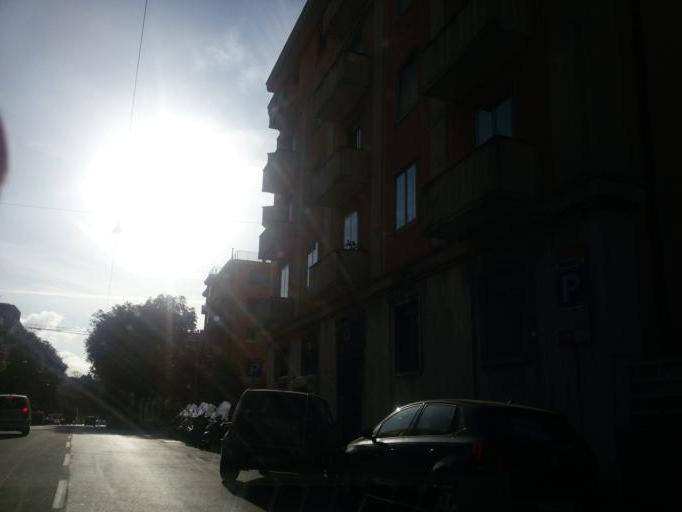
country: IT
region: Liguria
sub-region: Provincia di Genova
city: San Teodoro
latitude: 44.3945
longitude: 8.9651
